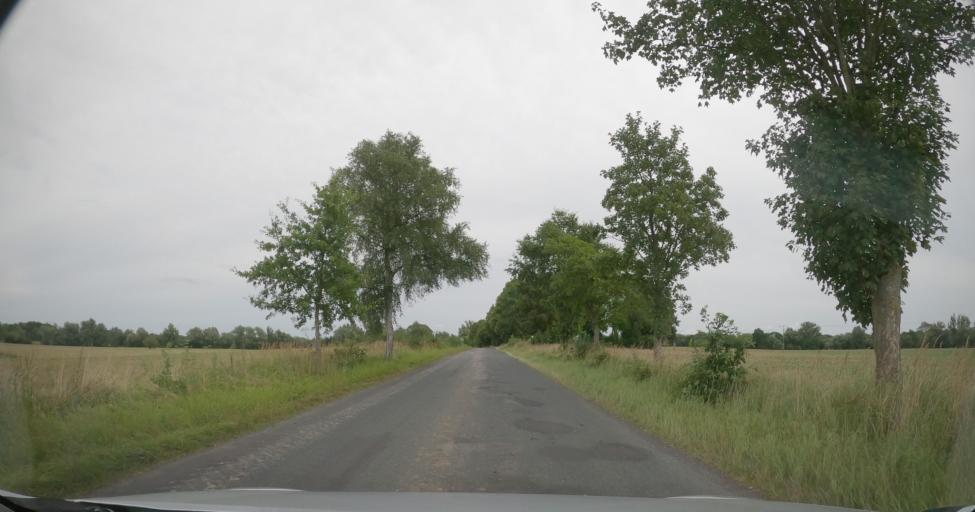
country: PL
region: West Pomeranian Voivodeship
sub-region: Powiat kamienski
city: Golczewo
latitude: 53.7828
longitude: 14.9139
